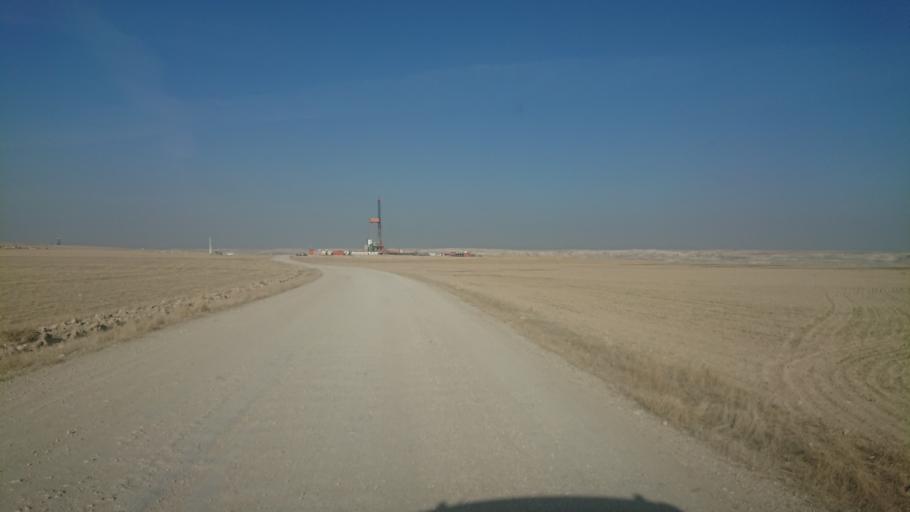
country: TR
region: Aksaray
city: Sultanhani
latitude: 38.0546
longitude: 33.6133
